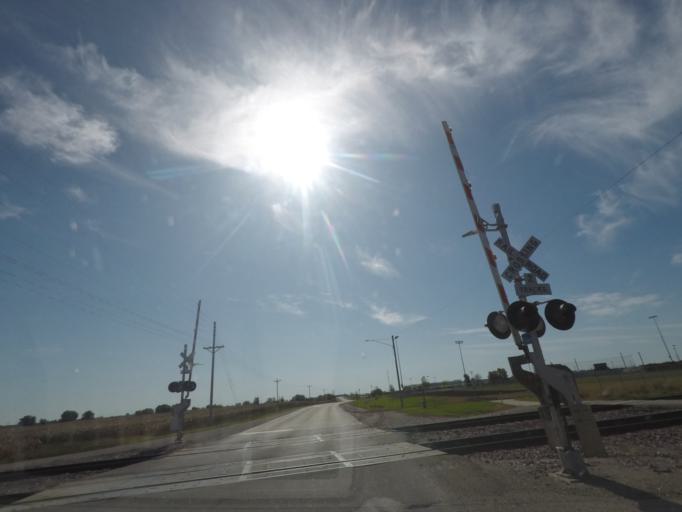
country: US
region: Iowa
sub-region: Story County
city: Nevada
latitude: 42.0165
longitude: -93.4347
